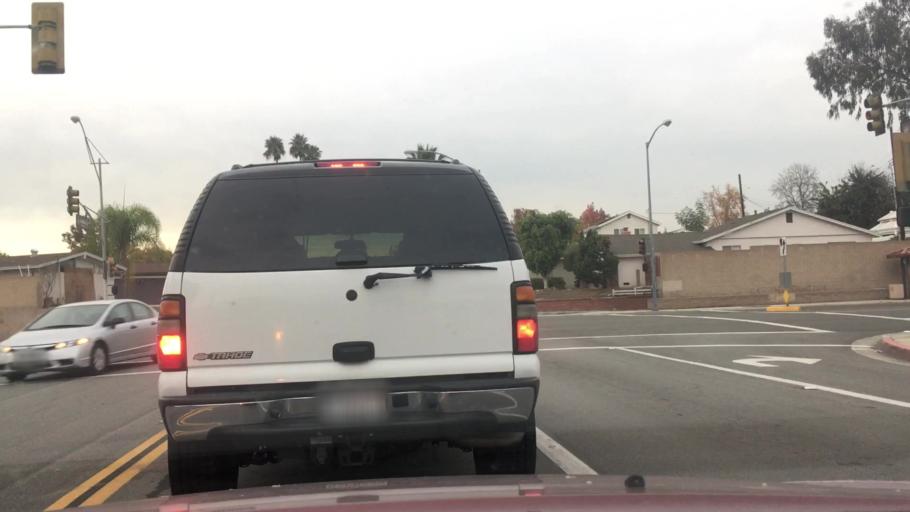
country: US
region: California
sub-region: Los Angeles County
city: La Mirada
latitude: 33.8985
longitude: -118.0051
